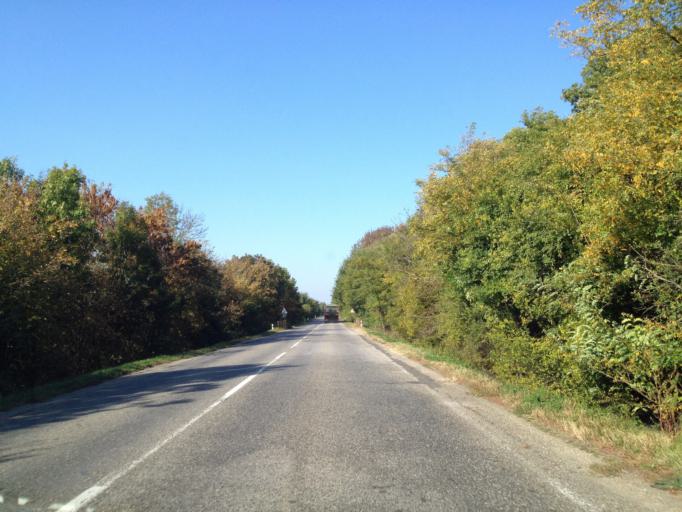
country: SK
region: Nitriansky
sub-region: Okres Komarno
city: Hurbanovo
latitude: 47.9241
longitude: 18.2333
